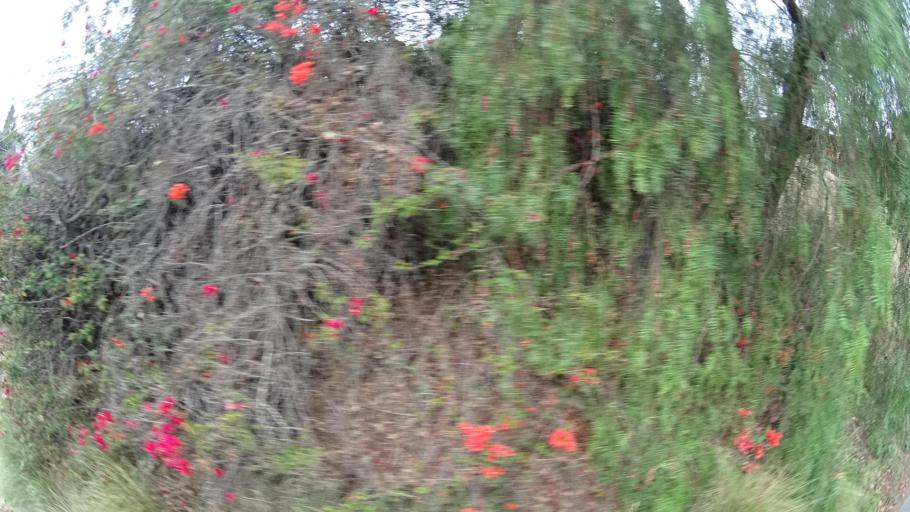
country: US
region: California
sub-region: San Diego County
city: Spring Valley
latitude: 32.7489
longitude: -117.0068
